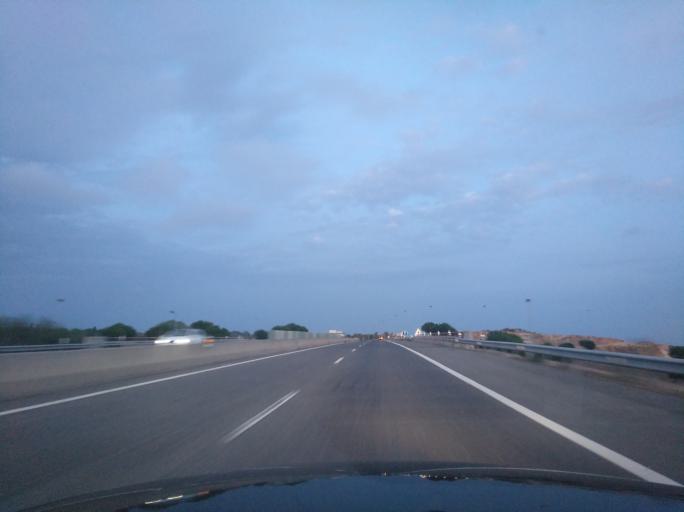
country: PT
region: Faro
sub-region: Portimao
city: Alvor
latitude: 37.1727
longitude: -8.6345
